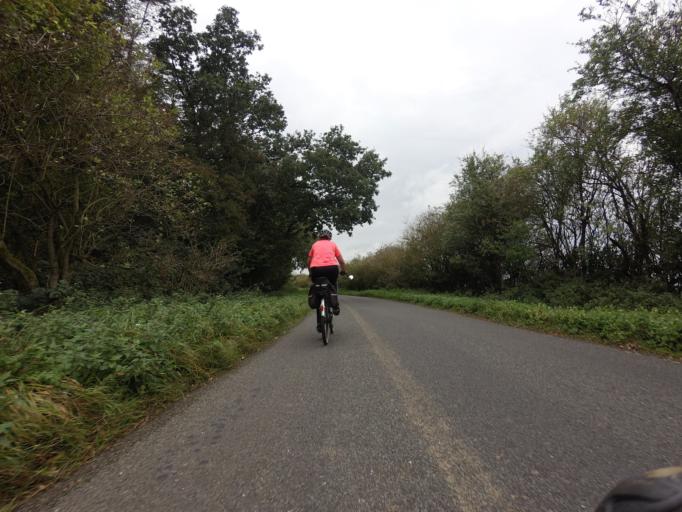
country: GB
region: England
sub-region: Cambridgeshire
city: Duxford
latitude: 52.0379
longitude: 0.1827
